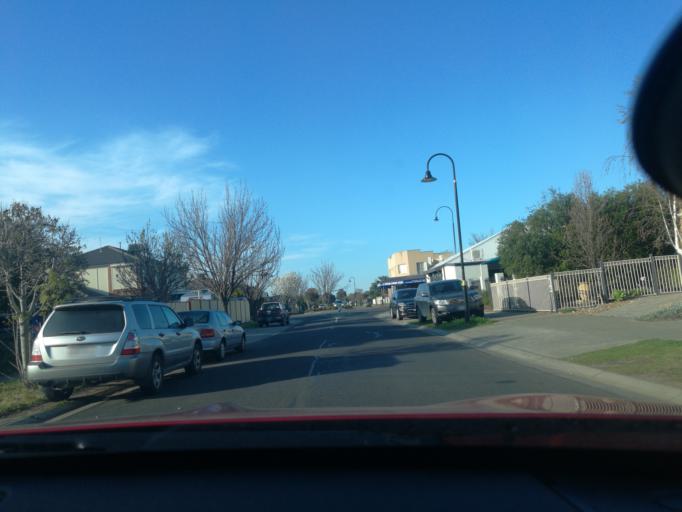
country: AU
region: Victoria
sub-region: Wyndham
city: Williams Landing
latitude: -37.8801
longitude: 144.7443
